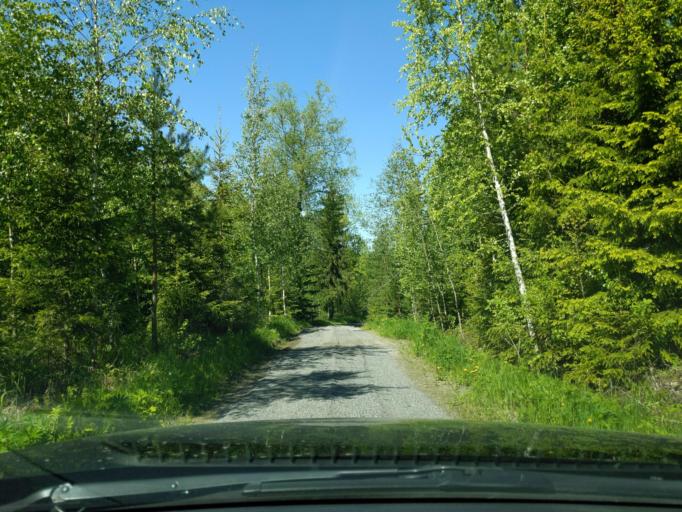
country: FI
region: Paijanne Tavastia
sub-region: Lahti
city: Lahti
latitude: 61.0545
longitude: 25.6898
